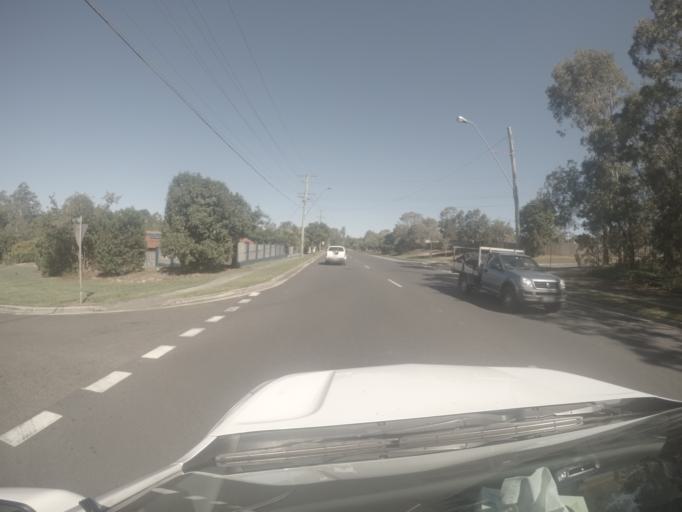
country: AU
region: Queensland
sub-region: Ipswich
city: Springfield
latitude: -27.6388
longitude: 152.9169
